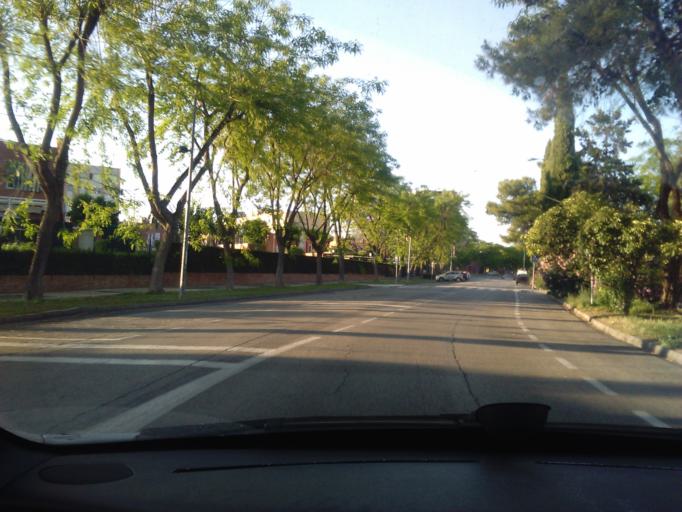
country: ES
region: Andalusia
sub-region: Provincia de Sevilla
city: Sevilla
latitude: 37.4063
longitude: -5.9461
